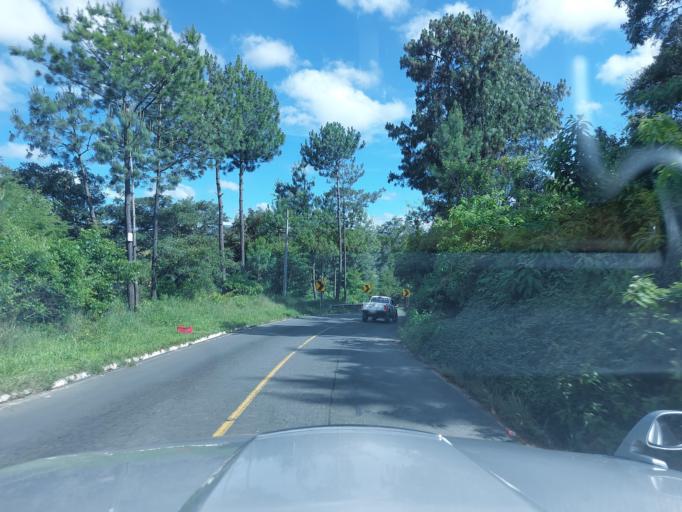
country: GT
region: Chimaltenango
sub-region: Municipio de Santa Cruz Balanya
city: Santa Cruz Balanya
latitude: 14.6817
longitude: -90.8956
